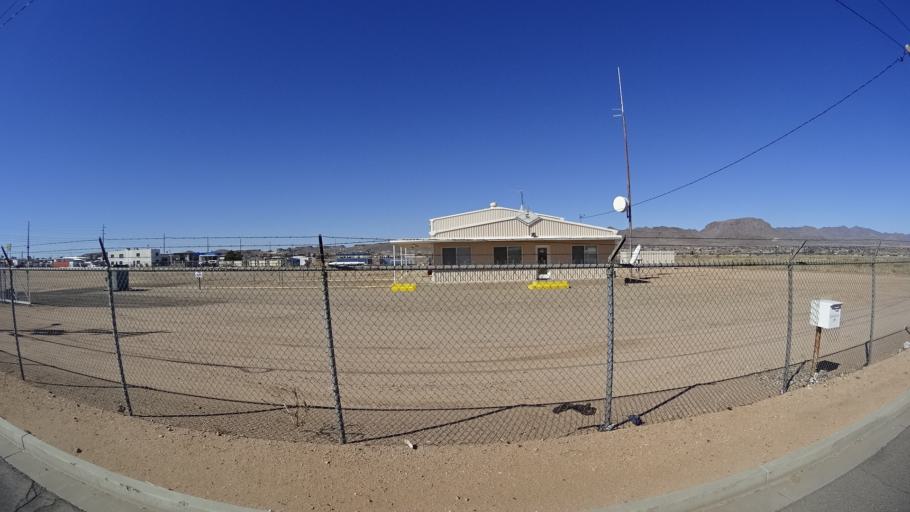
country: US
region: Arizona
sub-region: Mohave County
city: New Kingman-Butler
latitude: 35.2265
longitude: -114.0056
